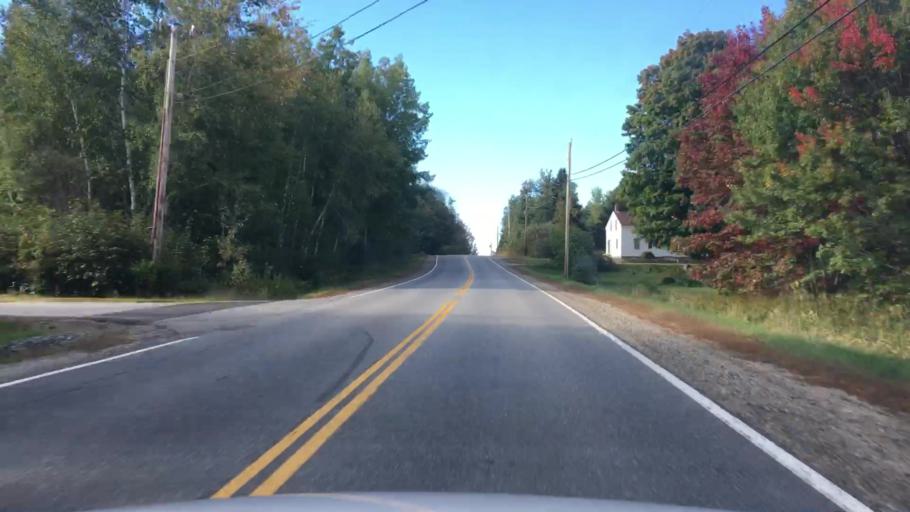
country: US
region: Maine
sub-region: Sagadahoc County
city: Topsham
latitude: 43.9426
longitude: -70.0266
